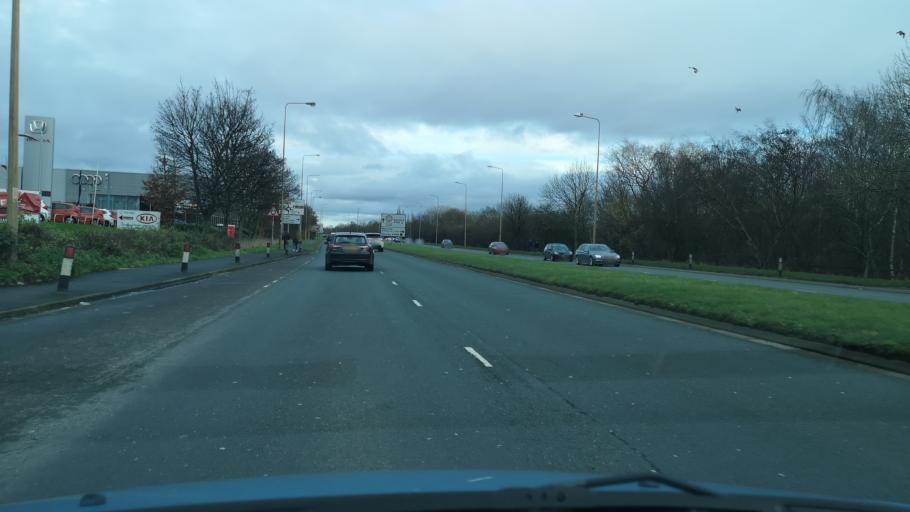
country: GB
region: England
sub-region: City and Borough of Wakefield
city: Crigglestone
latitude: 53.6560
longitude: -1.5152
